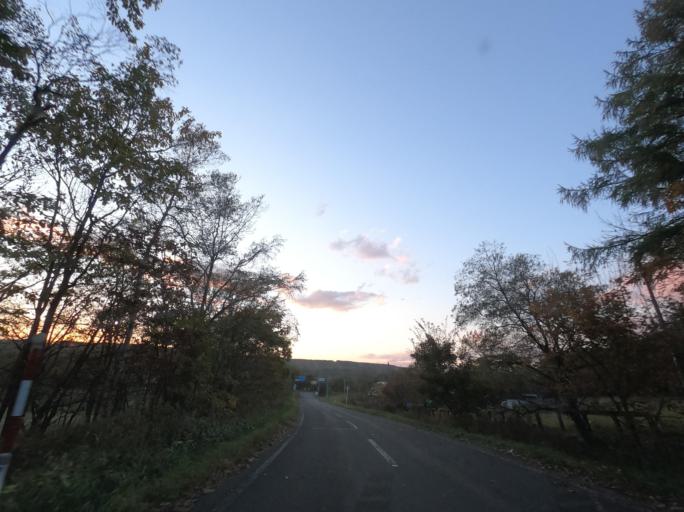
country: JP
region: Hokkaido
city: Kushiro
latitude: 43.2256
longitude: 144.4380
